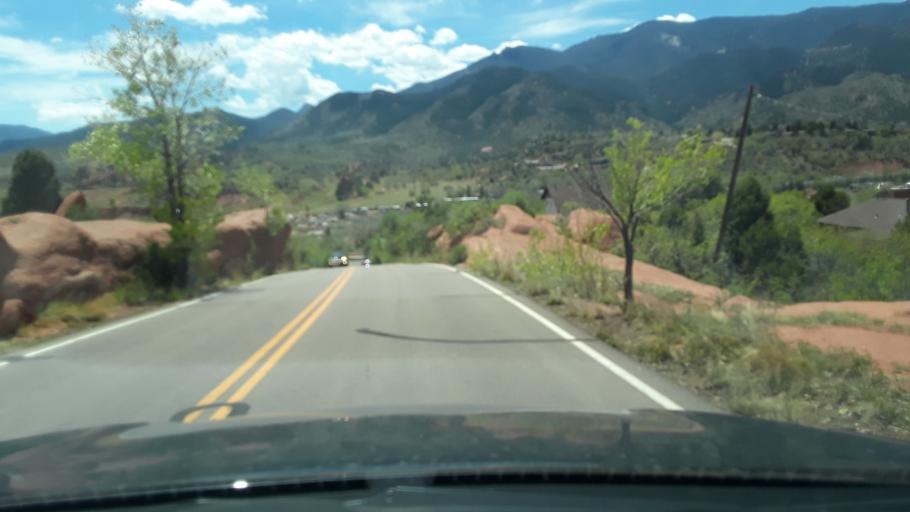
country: US
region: Colorado
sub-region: El Paso County
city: Manitou Springs
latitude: 38.8595
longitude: -104.8805
